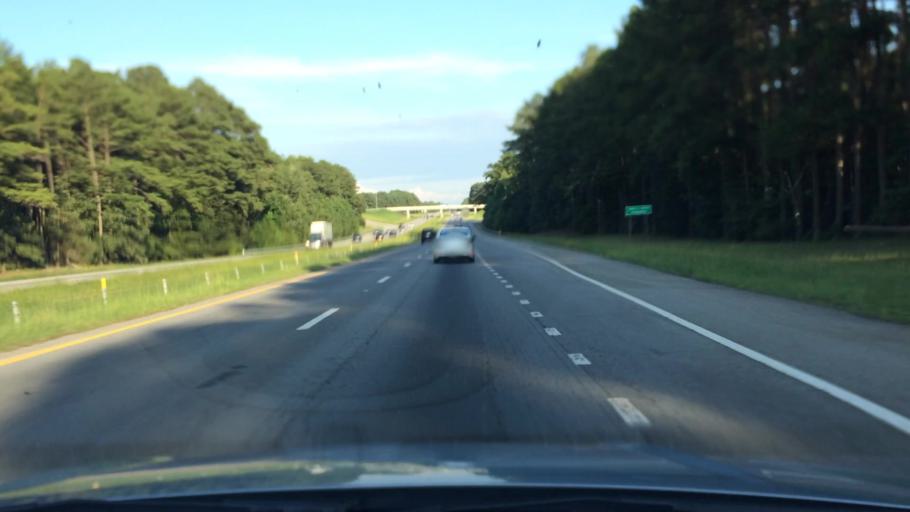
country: US
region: South Carolina
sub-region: Newberry County
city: Newberry
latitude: 34.3143
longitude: -81.5801
